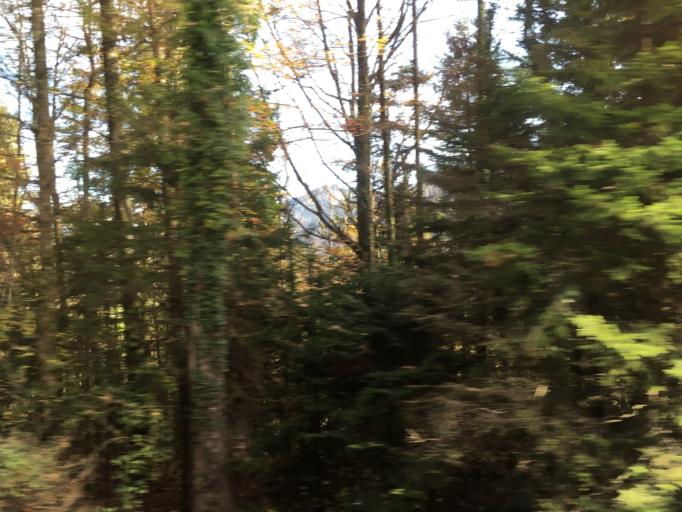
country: CH
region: Schwyz
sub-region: Bezirk Schwyz
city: Goldau
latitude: 47.0525
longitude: 8.5669
